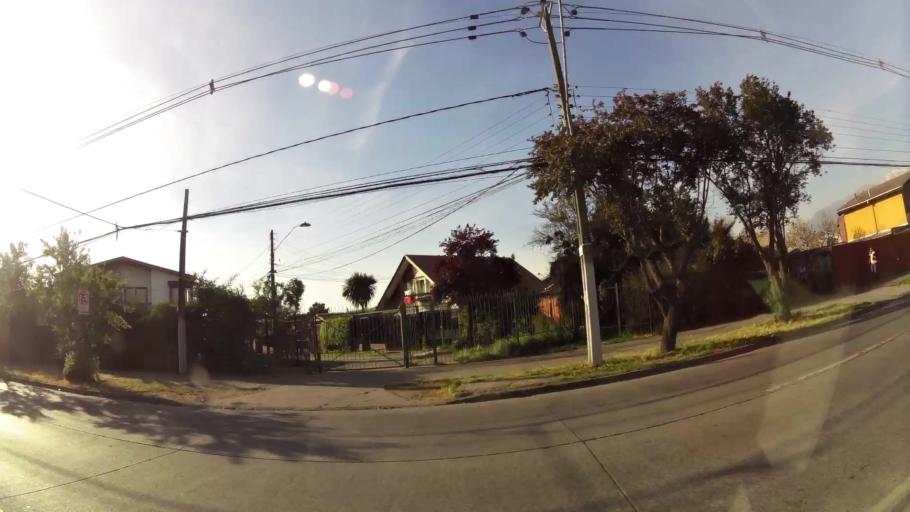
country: CL
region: Santiago Metropolitan
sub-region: Provincia de Santiago
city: La Pintana
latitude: -33.5533
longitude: -70.5844
